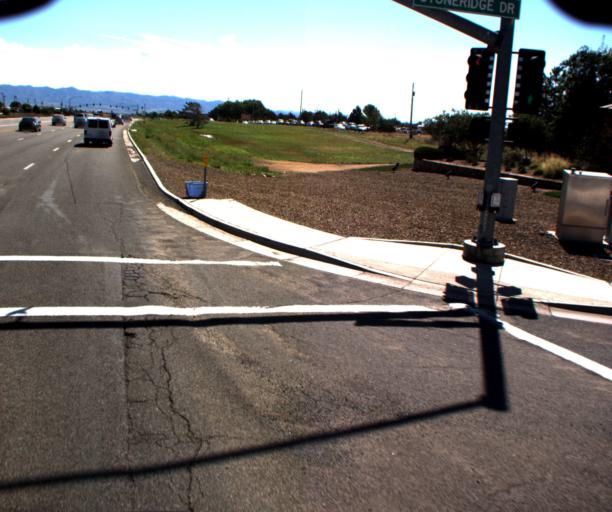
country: US
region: Arizona
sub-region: Yavapai County
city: Prescott Valley
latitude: 34.5795
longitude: -112.3602
